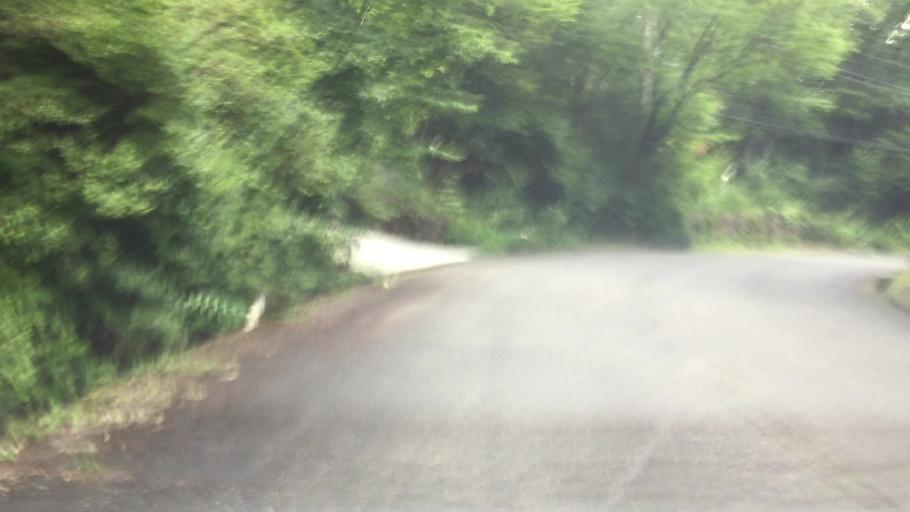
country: JP
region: Tochigi
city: Kuroiso
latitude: 37.1049
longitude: 140.0421
